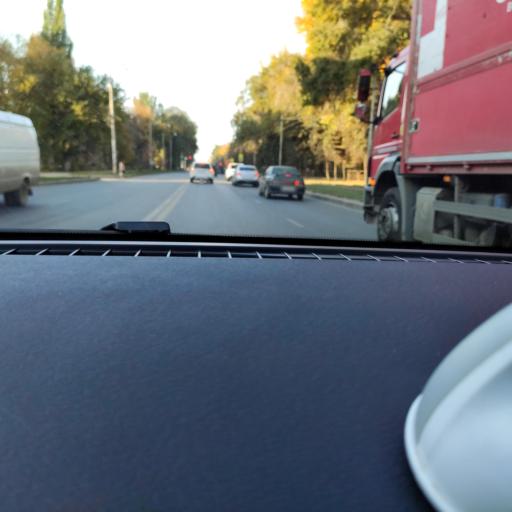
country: RU
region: Samara
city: Samara
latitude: 53.2004
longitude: 50.2262
